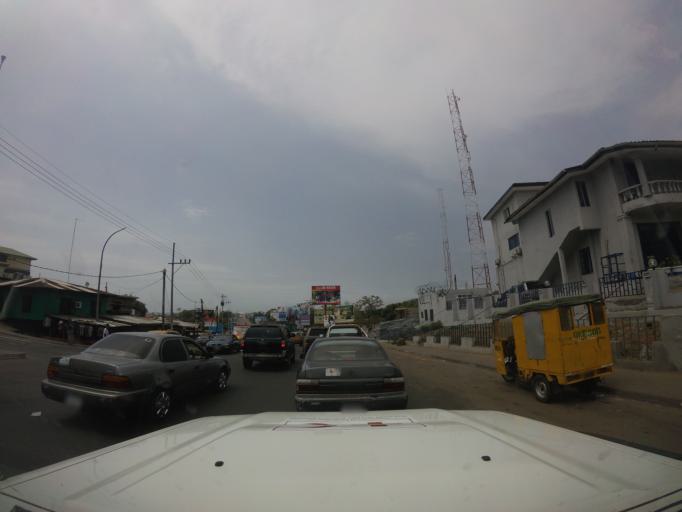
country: LR
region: Montserrado
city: Monrovia
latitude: 6.3164
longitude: -10.8014
